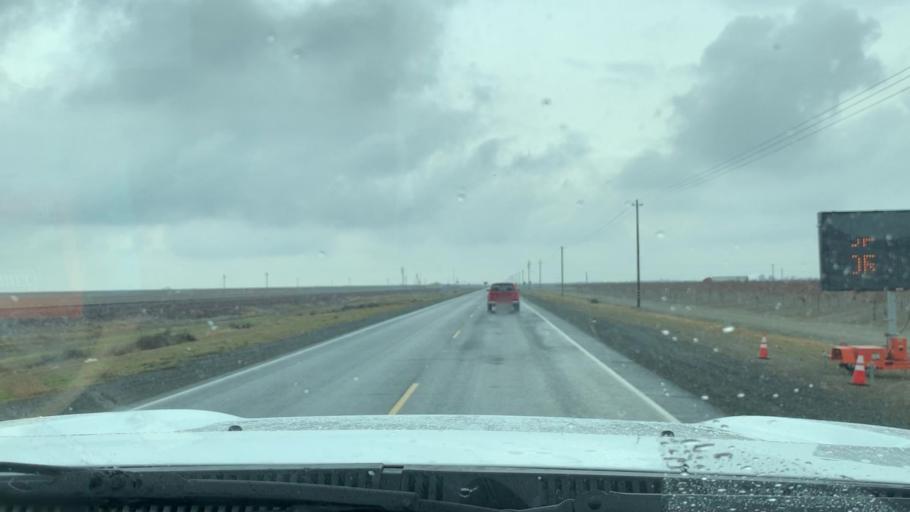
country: US
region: California
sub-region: Tulare County
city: Alpaugh
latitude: 36.0045
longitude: -119.4877
